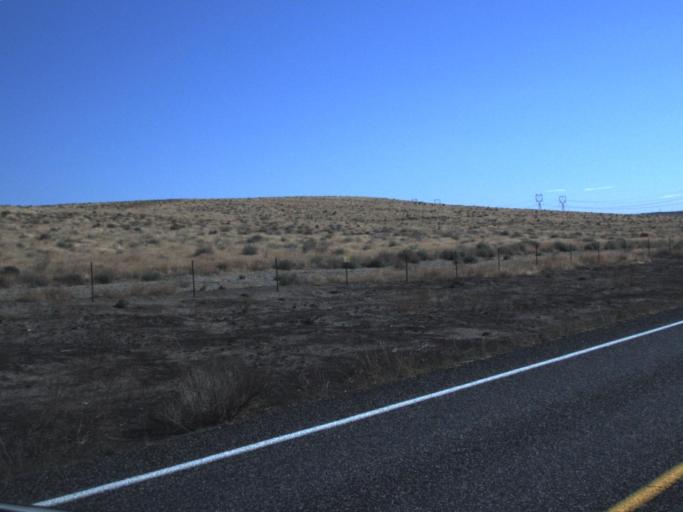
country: US
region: Washington
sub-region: Grant County
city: Desert Aire
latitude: 46.5652
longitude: -119.7187
